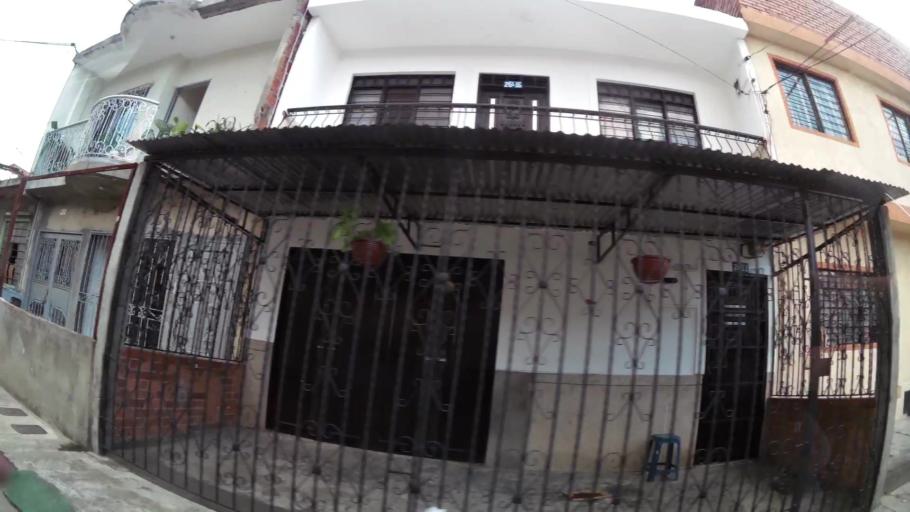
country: CO
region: Valle del Cauca
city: Cali
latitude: 3.4161
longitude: -76.5188
